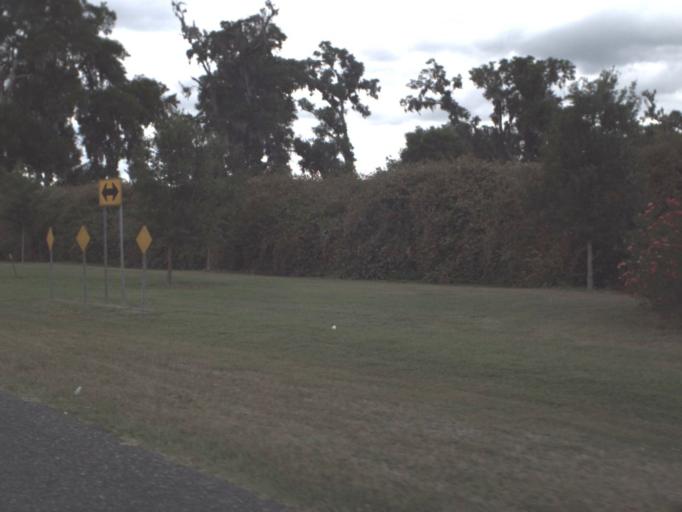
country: US
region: Florida
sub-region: Marion County
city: Ocala
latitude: 29.2595
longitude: -82.1476
